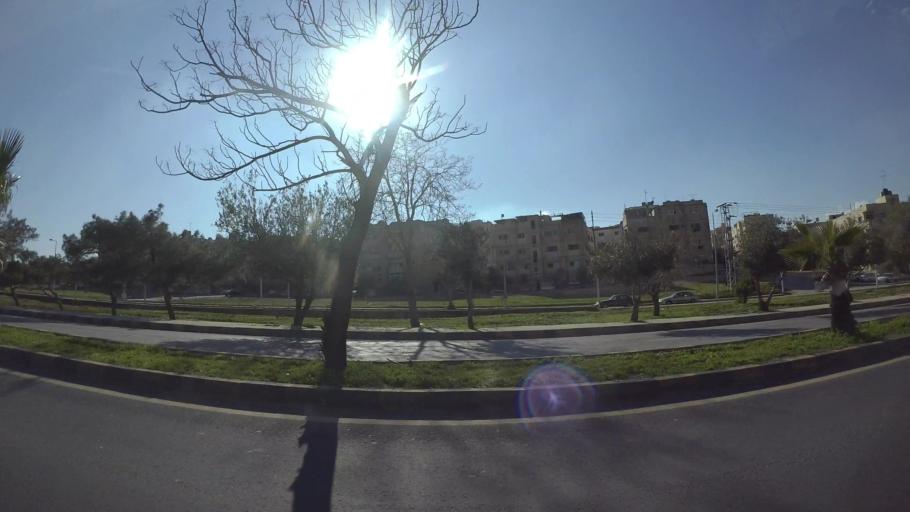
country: JO
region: Amman
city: Amman
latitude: 31.9762
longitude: 35.9340
